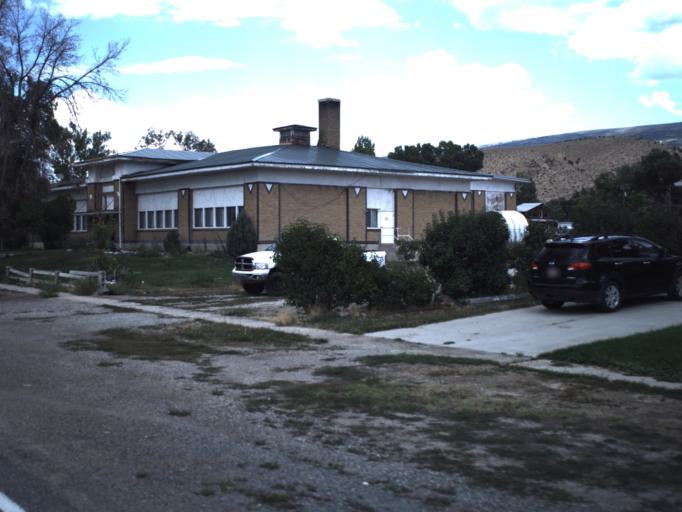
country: US
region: Utah
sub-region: Sanpete County
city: Centerfield
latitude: 39.1132
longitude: -111.7088
